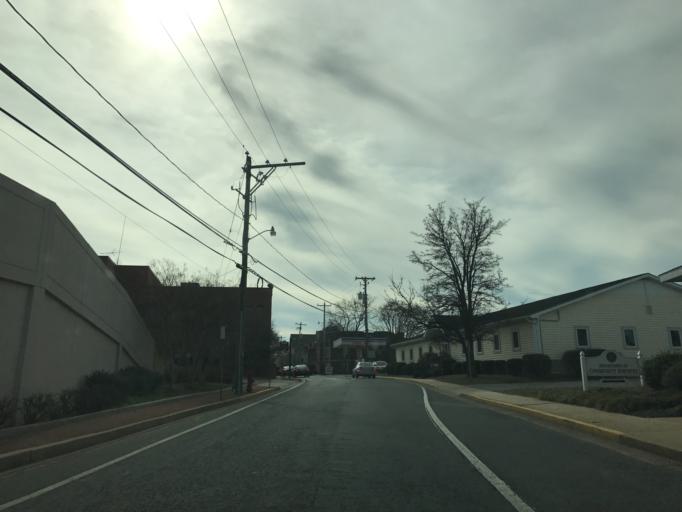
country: US
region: Maryland
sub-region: Queen Anne's County
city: Centreville
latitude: 39.0465
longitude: -76.0649
